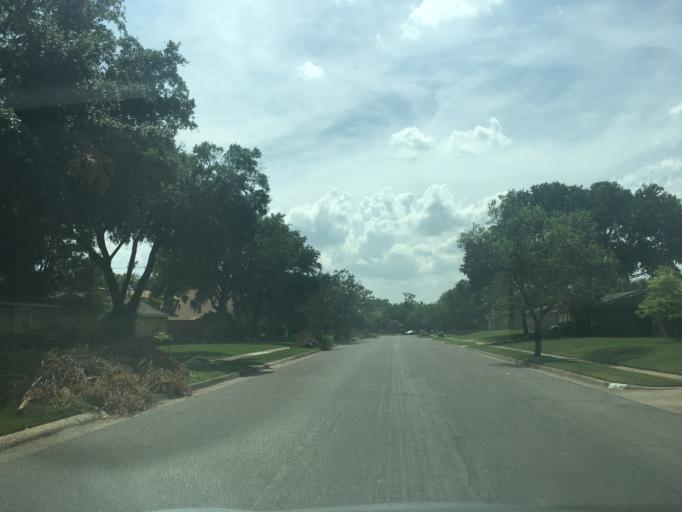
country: US
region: Texas
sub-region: Dallas County
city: Farmers Branch
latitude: 32.9130
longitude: -96.8527
